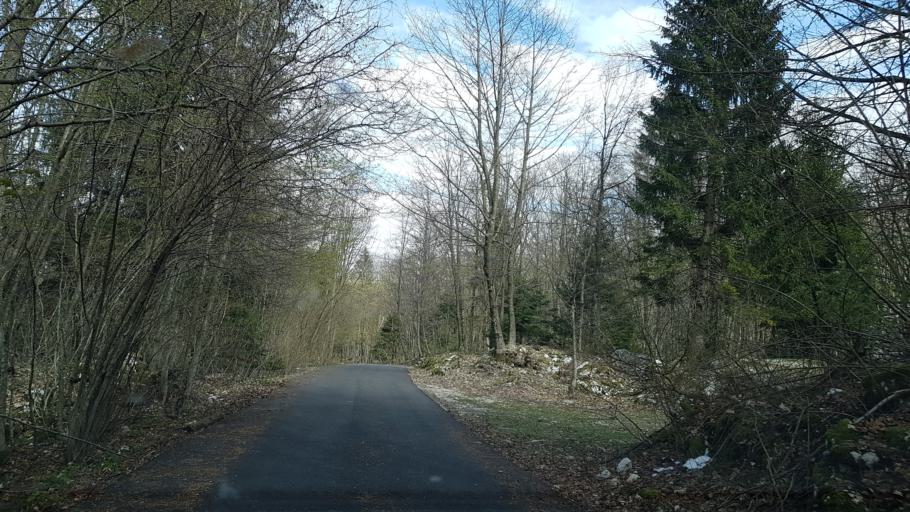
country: IT
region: Friuli Venezia Giulia
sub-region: Provincia di Udine
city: Trasaghis
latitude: 46.2863
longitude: 13.0156
